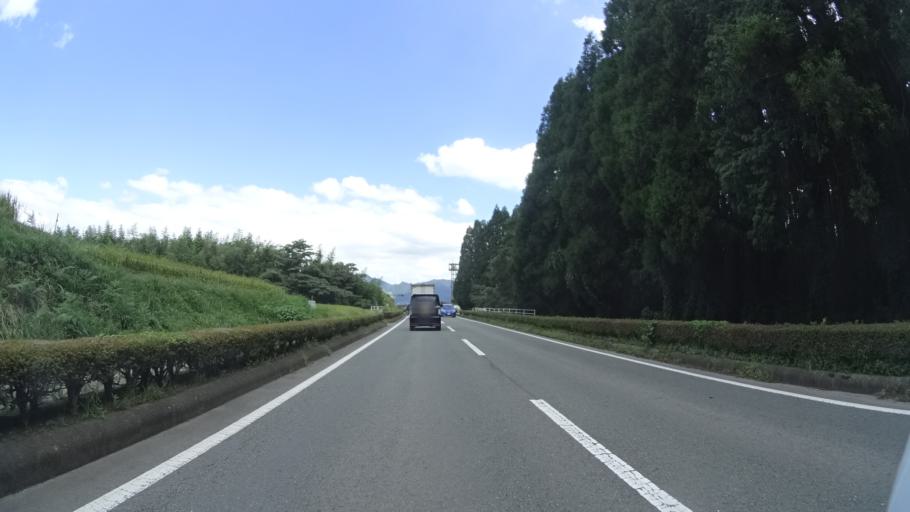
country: JP
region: Kumamoto
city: Aso
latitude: 32.8304
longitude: 131.0869
